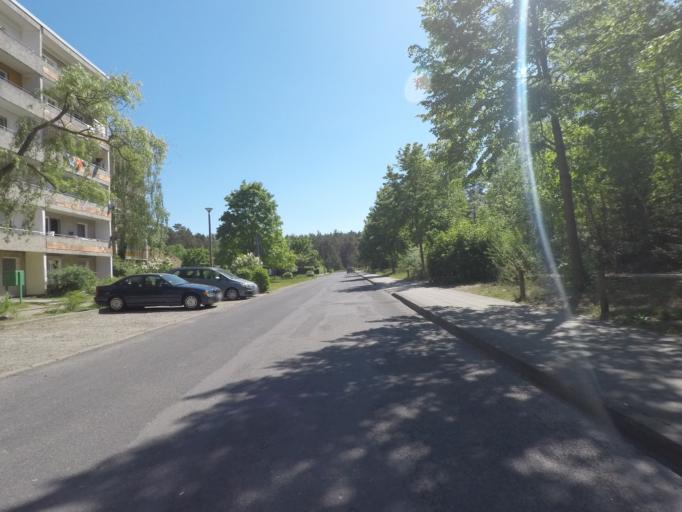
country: DE
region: Brandenburg
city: Eberswalde
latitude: 52.8292
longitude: 13.7592
